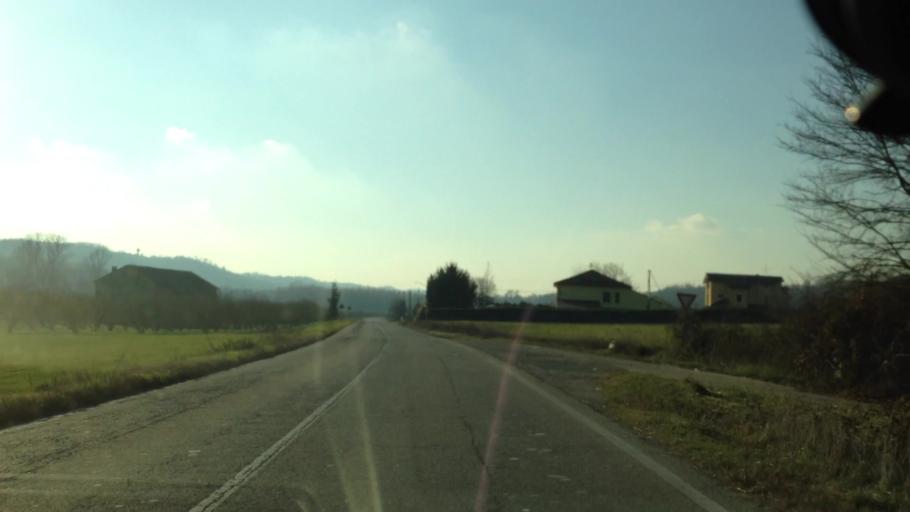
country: IT
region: Piedmont
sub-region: Provincia di Asti
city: Incisa Scapaccino
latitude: 44.8388
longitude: 8.3858
